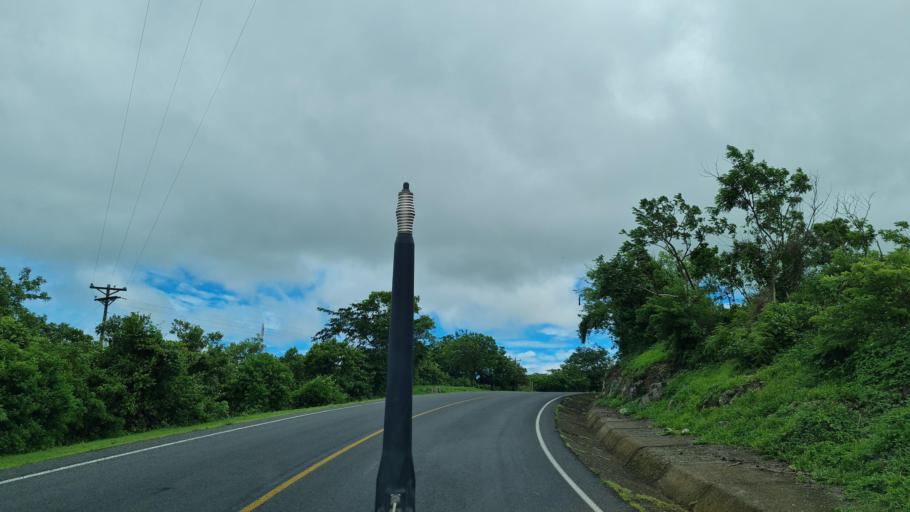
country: NI
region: Matagalpa
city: Terrabona
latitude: 12.5847
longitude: -85.9810
